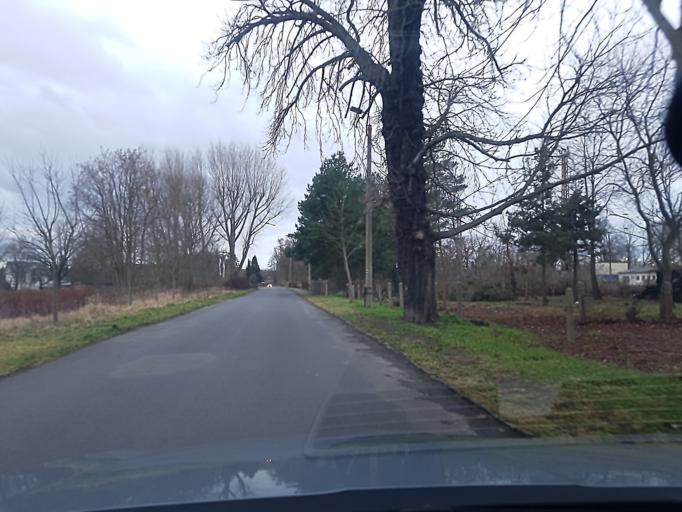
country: DE
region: Brandenburg
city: Doberlug-Kirchhain
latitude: 51.6193
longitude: 13.5594
